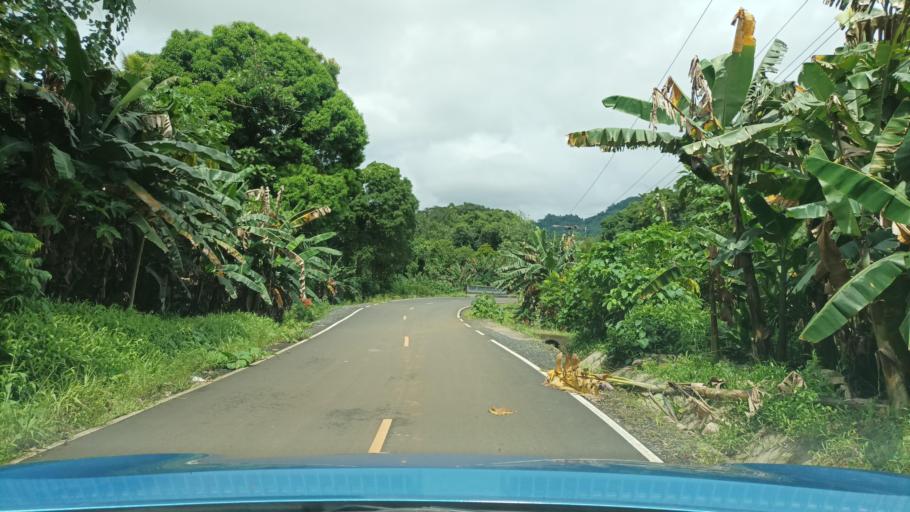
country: FM
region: Pohnpei
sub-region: Madolenihm Municipality
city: Madolenihm Municipality Government
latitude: 6.8833
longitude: 158.3216
